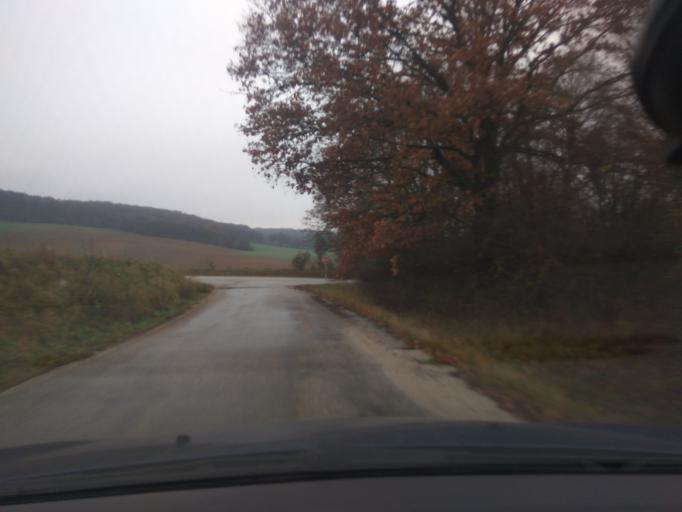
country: SK
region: Trnavsky
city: Vrbove
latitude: 48.6872
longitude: 17.6716
